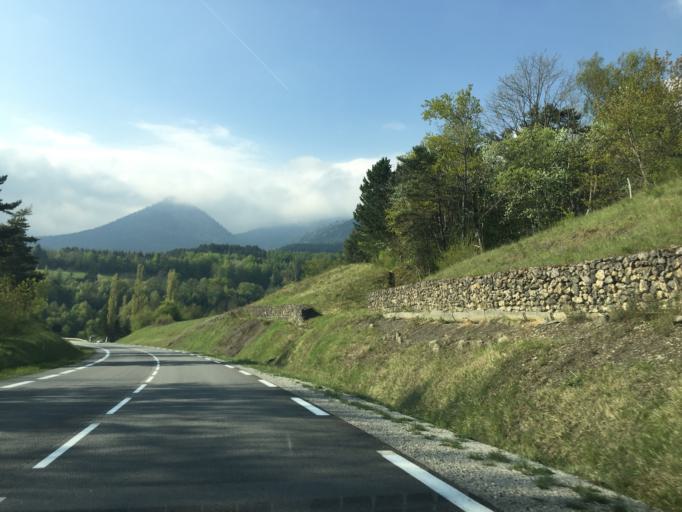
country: FR
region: Rhone-Alpes
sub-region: Departement de l'Isere
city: Mens
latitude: 44.7909
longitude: 5.6336
